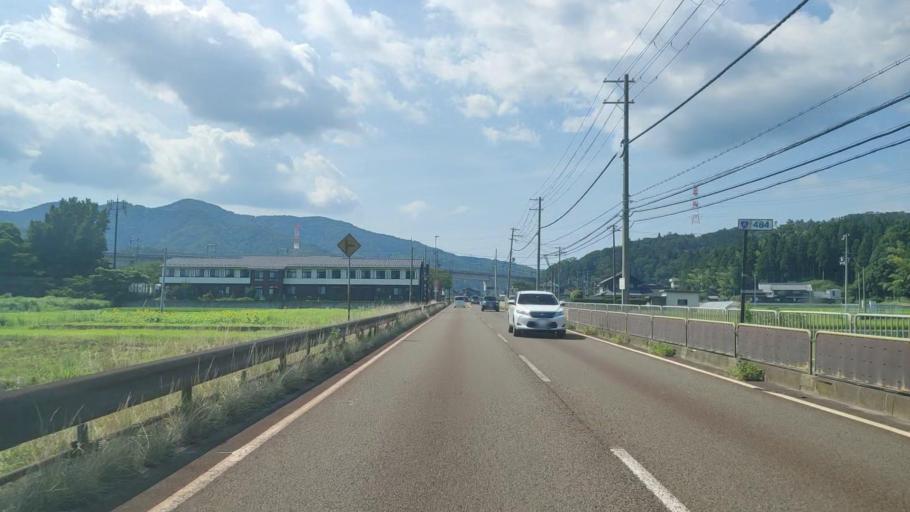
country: JP
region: Fukui
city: Tsuruga
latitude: 35.5267
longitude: 136.1587
